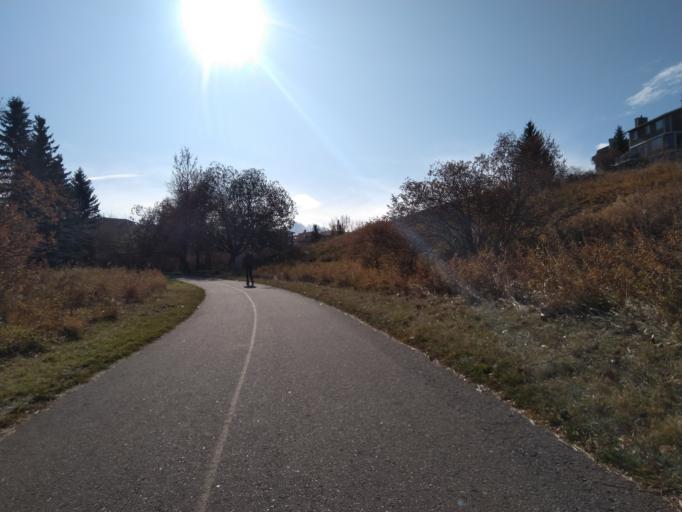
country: CA
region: Alberta
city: Calgary
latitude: 51.1359
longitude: -114.1486
